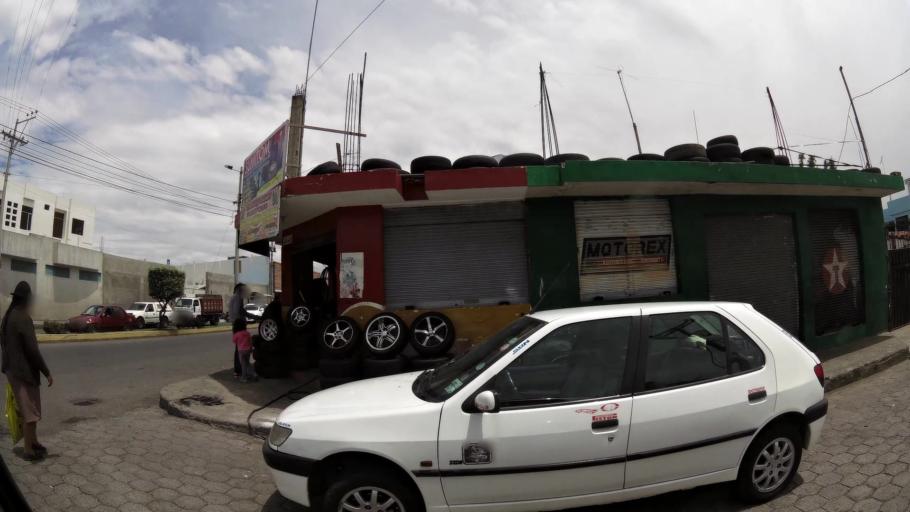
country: EC
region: Cotopaxi
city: San Miguel de Salcedo
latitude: -1.0481
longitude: -78.5933
